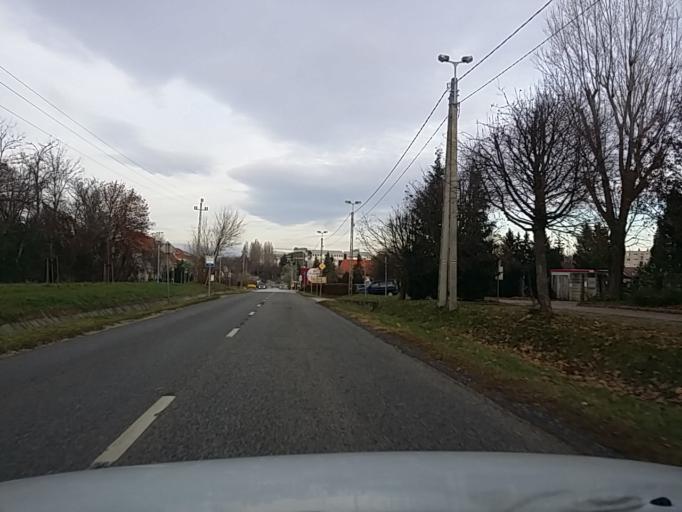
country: HU
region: Veszprem
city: Veszprem
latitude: 47.0818
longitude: 17.8961
